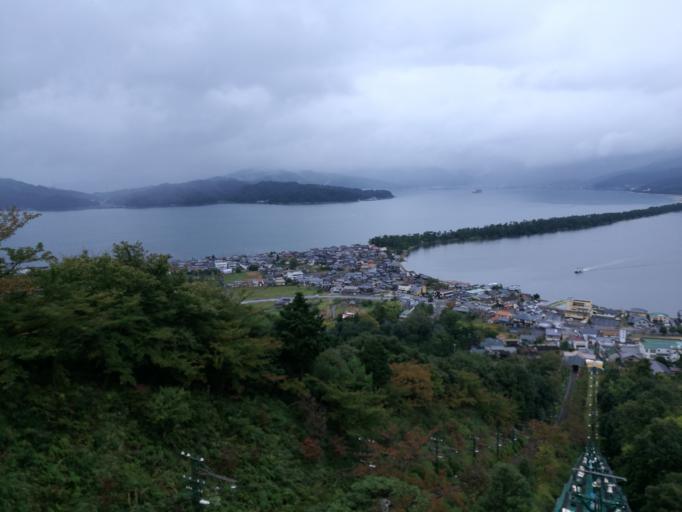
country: JP
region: Kyoto
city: Miyazu
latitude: 35.5862
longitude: 135.1956
